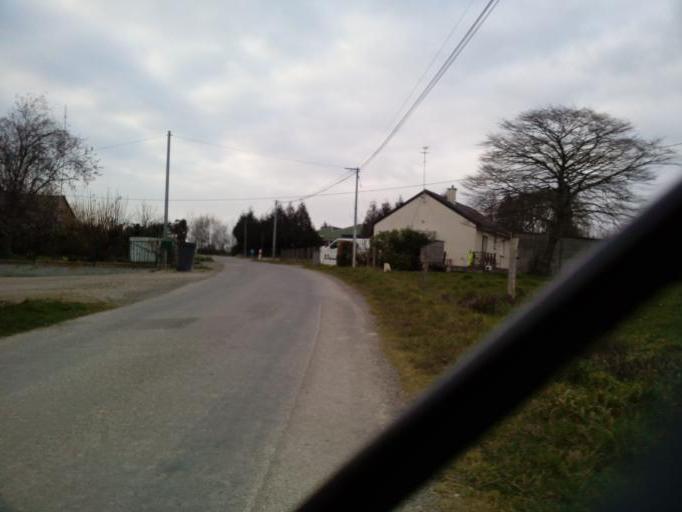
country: FR
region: Brittany
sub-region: Departement d'Ille-et-Vilaine
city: Talensac
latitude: 48.1140
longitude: -1.9028
